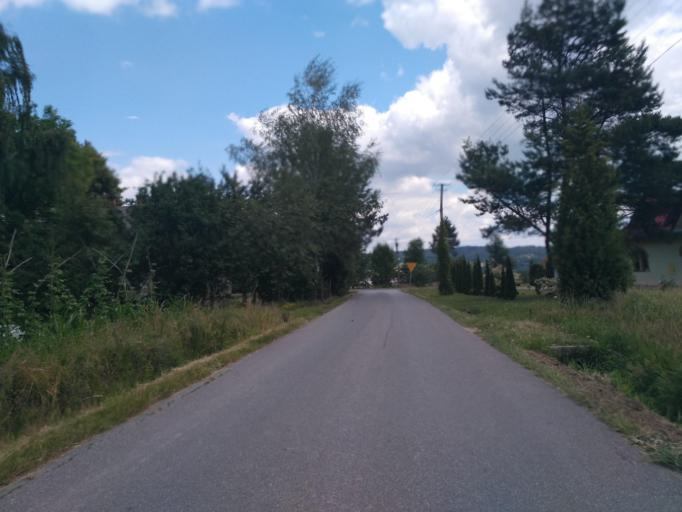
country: PL
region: Subcarpathian Voivodeship
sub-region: Powiat jasielski
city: Brzyska
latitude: 49.8149
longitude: 21.3944
